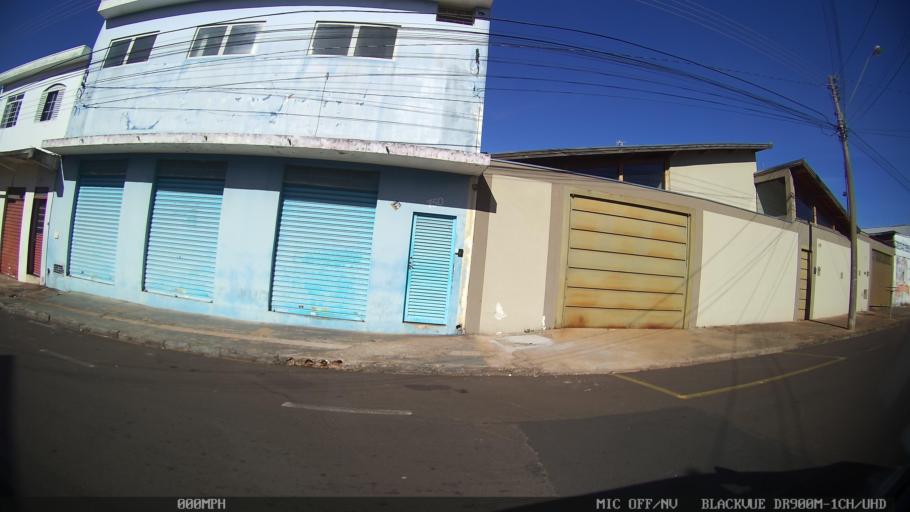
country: BR
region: Sao Paulo
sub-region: Franca
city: Franca
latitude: -20.5316
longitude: -47.4082
